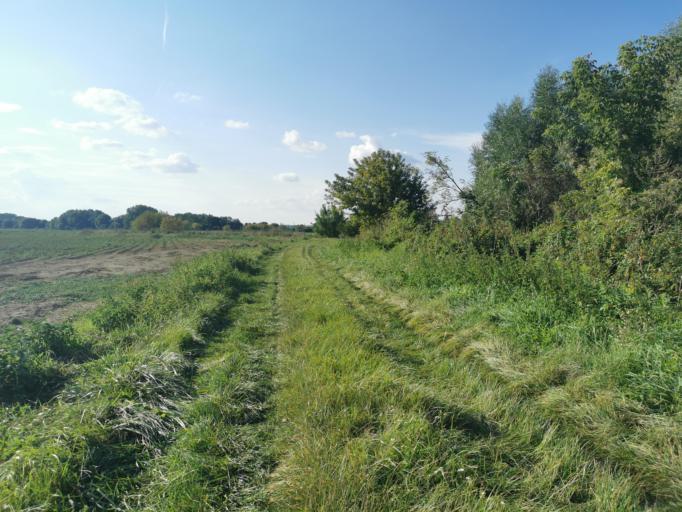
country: SK
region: Trnavsky
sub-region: Okres Senica
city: Senica
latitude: 48.6624
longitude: 17.3102
